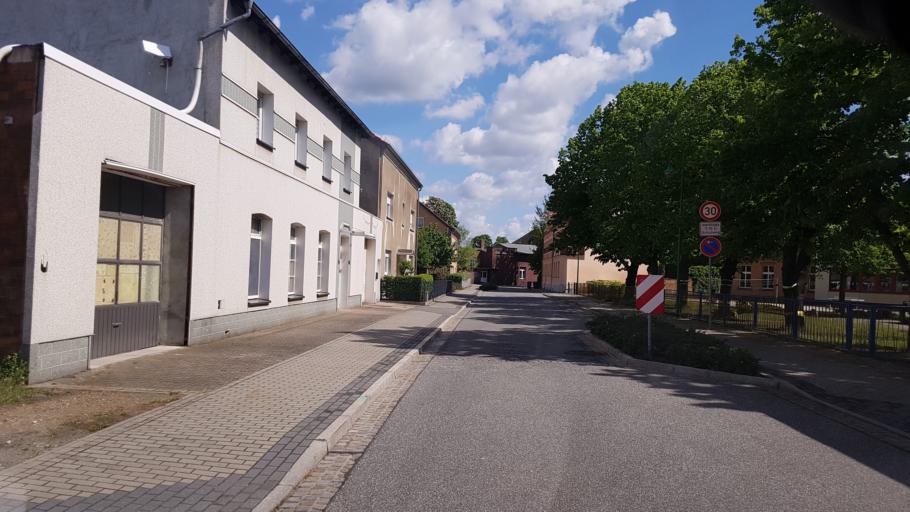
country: DE
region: Brandenburg
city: Grossraschen
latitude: 51.5835
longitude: 14.0050
